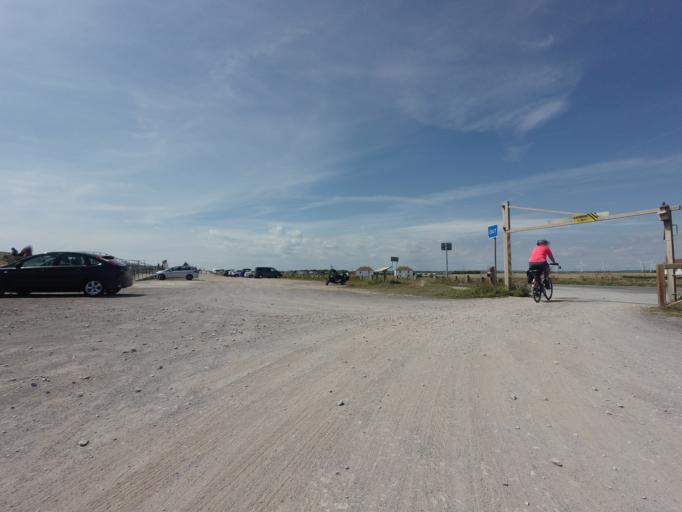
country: GB
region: England
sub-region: East Sussex
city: Rye
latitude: 50.9302
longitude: 0.8145
